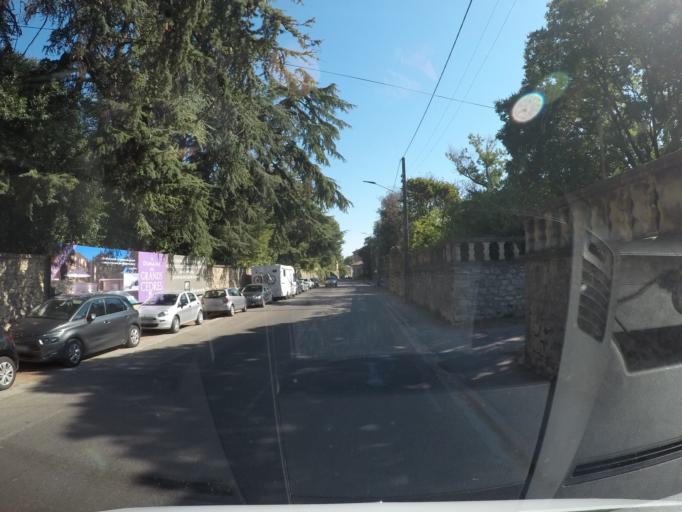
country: FR
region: Languedoc-Roussillon
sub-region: Departement du Gard
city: Uzes
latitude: 44.0107
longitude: 4.4099
